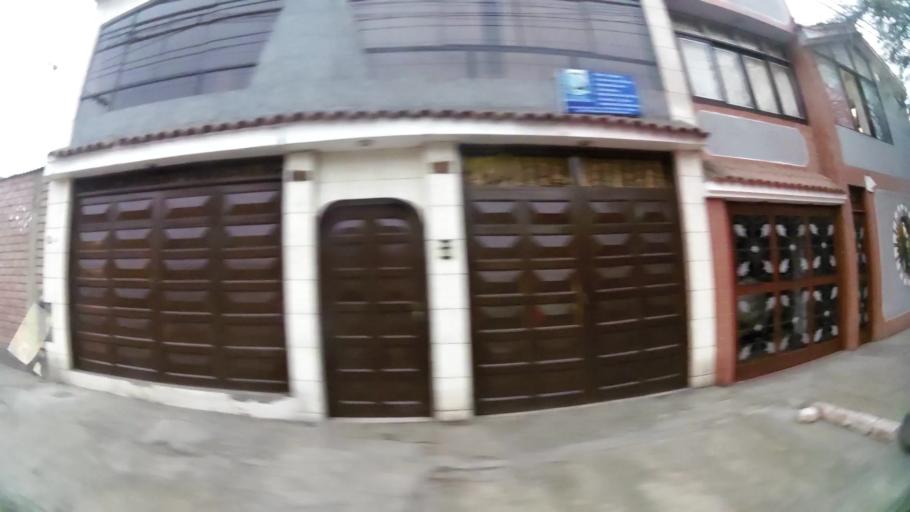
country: PE
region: Lima
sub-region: Lima
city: Surco
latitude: -12.1680
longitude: -76.9727
